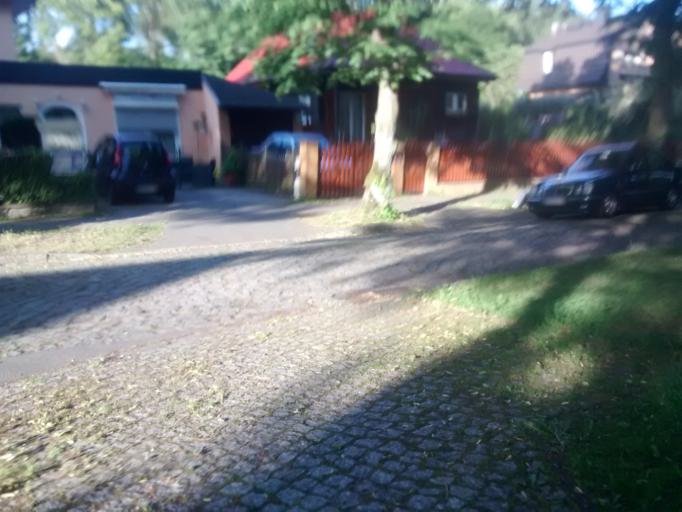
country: DE
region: Brandenburg
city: Birkenwerder
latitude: 52.6753
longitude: 13.2946
